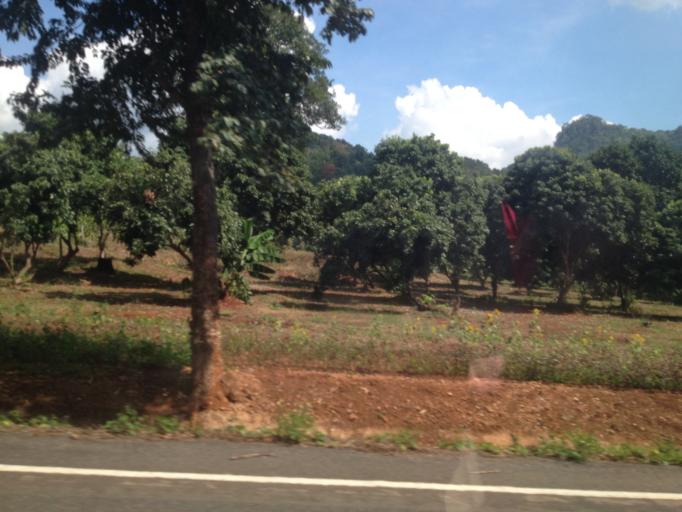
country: TH
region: Chiang Mai
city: Samoeng
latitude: 18.8082
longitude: 98.7898
